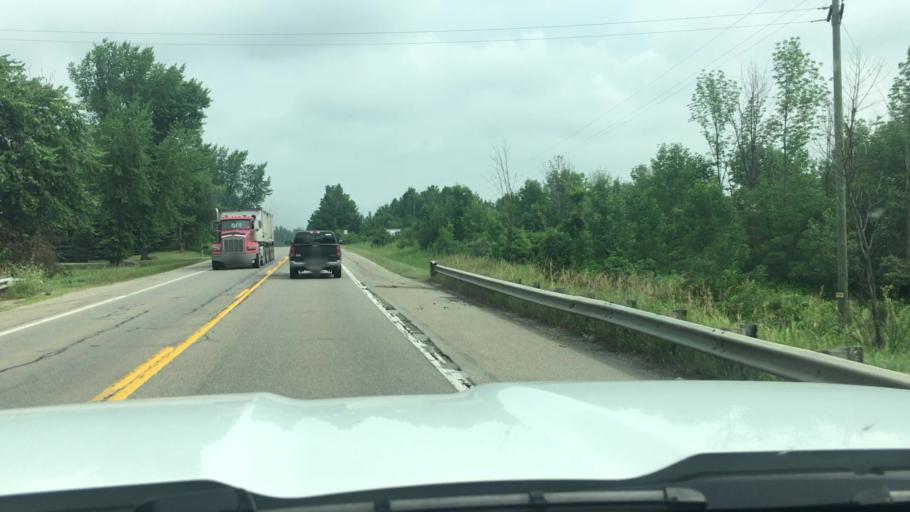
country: US
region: Michigan
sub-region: Sanilac County
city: Brown City
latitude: 43.1453
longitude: -83.0742
